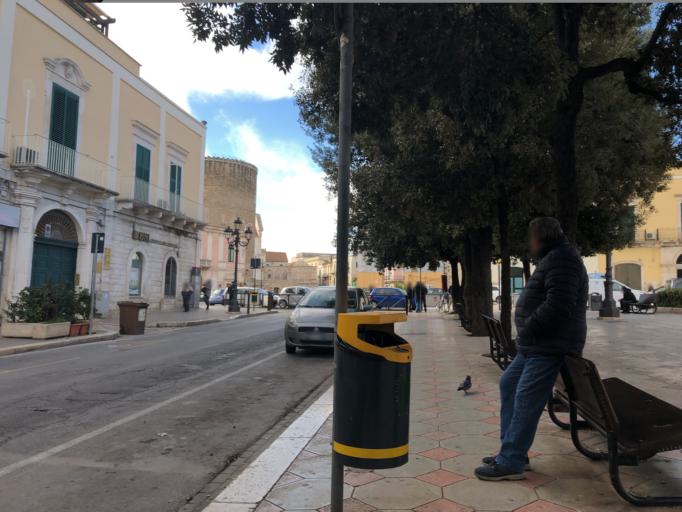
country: IT
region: Apulia
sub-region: Provincia di Bari
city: Bitonto
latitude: 41.1085
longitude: 16.6916
